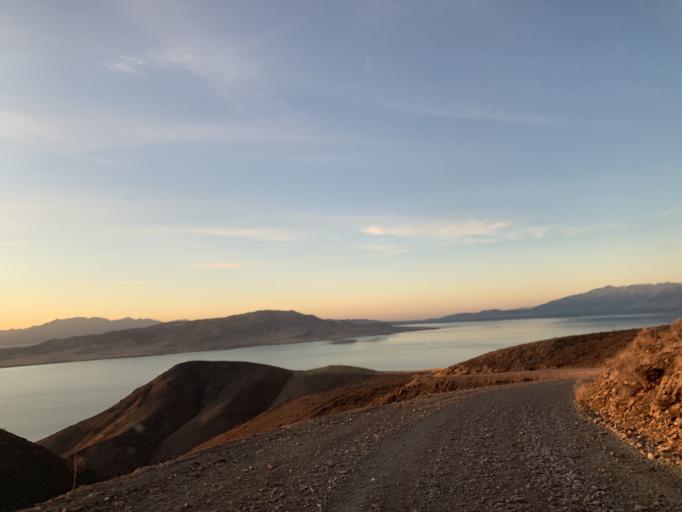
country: US
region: Utah
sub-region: Utah County
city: West Mountain
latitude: 40.1068
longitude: -111.8212
